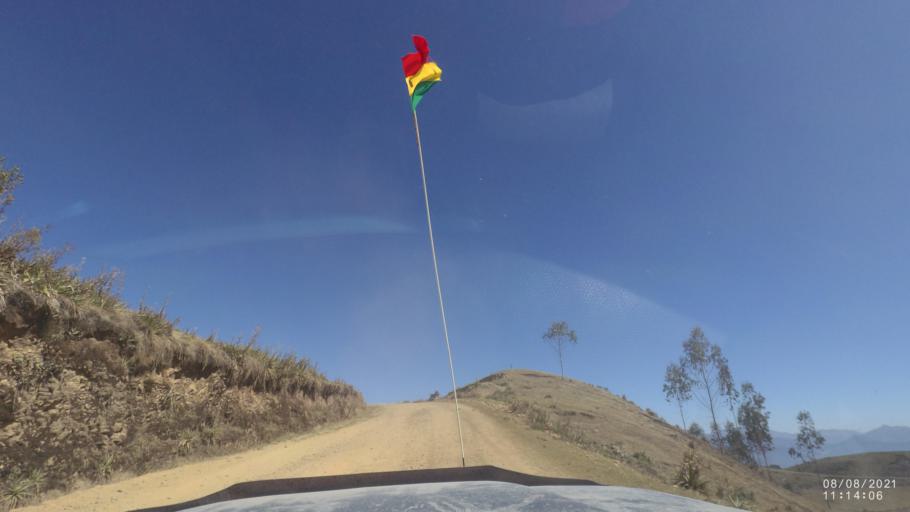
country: BO
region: Cochabamba
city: Colchani
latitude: -16.7690
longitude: -66.6657
